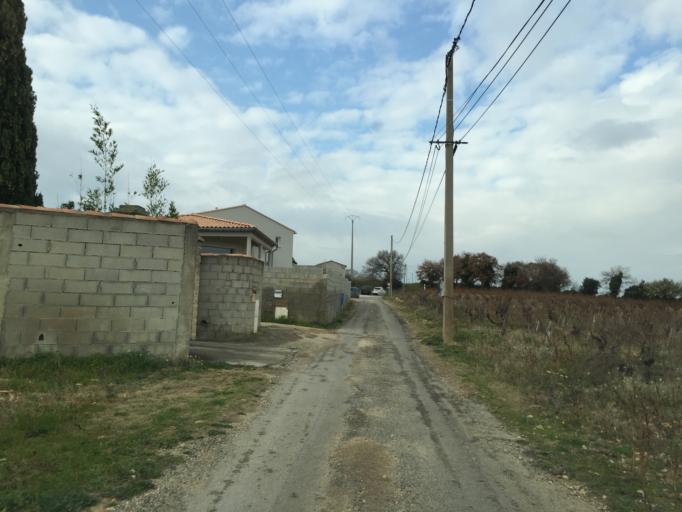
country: FR
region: Provence-Alpes-Cote d'Azur
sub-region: Departement du Vaucluse
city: Bedarrides
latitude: 44.0462
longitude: 4.8820
